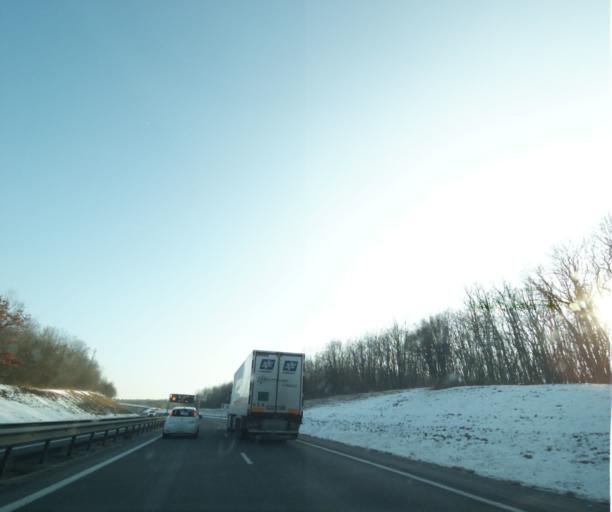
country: FR
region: Rhone-Alpes
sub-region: Departement de l'Ain
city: Bellegarde-sur-Valserine
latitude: 46.0772
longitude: 5.8435
